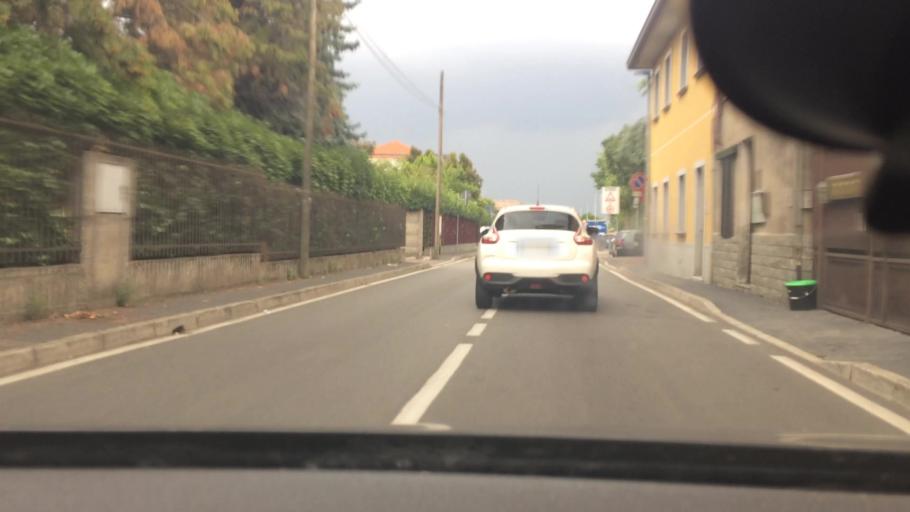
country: IT
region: Lombardy
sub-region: Citta metropolitana di Milano
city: Cantalupo
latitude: 45.5768
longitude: 8.9810
